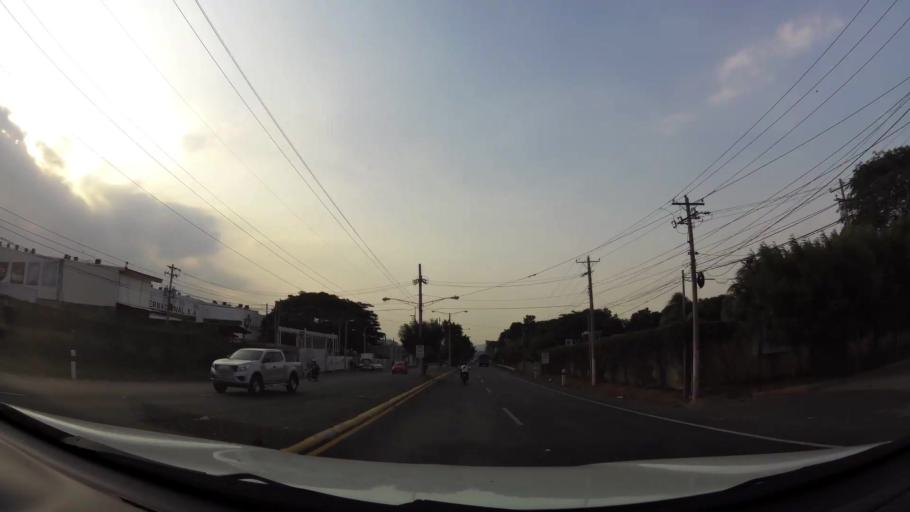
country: NI
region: Managua
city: Ciudad Sandino
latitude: 12.1458
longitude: -86.3354
